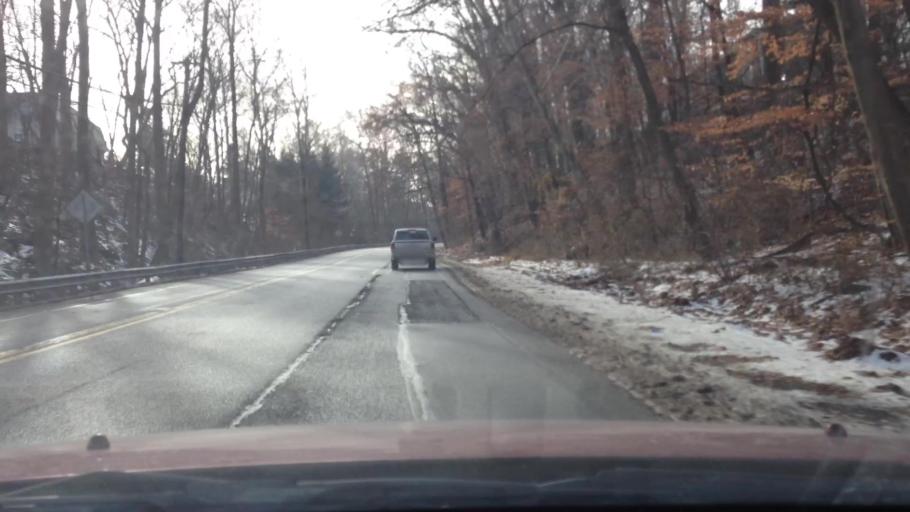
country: US
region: Pennsylvania
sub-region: Montgomery County
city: Narberth
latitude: 40.0367
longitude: -75.2547
